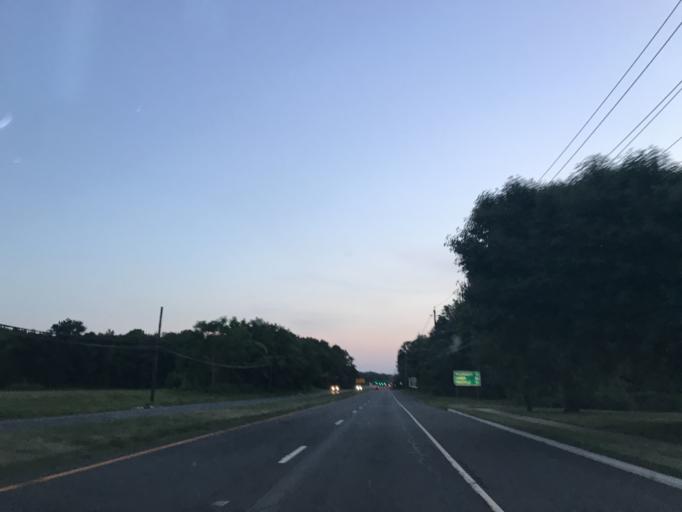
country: US
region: New Jersey
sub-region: Burlington County
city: Bordentown
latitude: 40.1304
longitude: -74.7285
